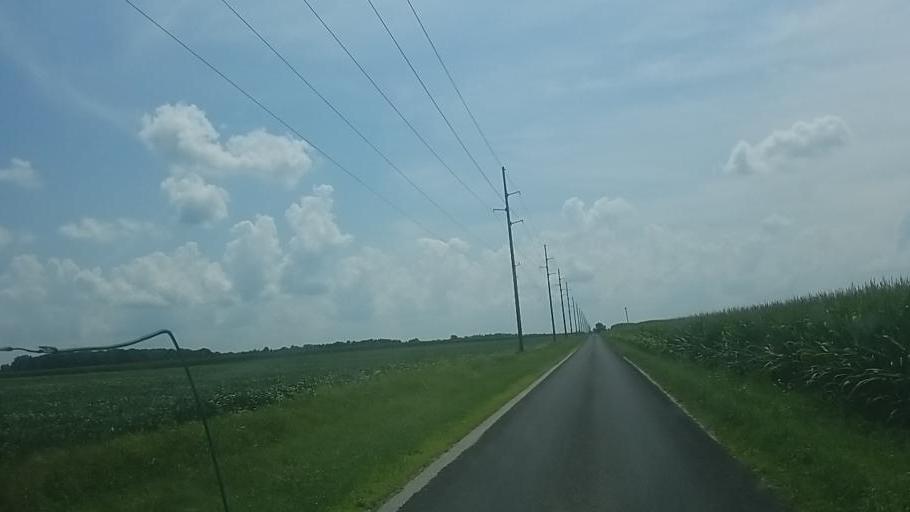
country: US
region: Ohio
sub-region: Wyandot County
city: Upper Sandusky
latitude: 40.6342
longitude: -83.3239
